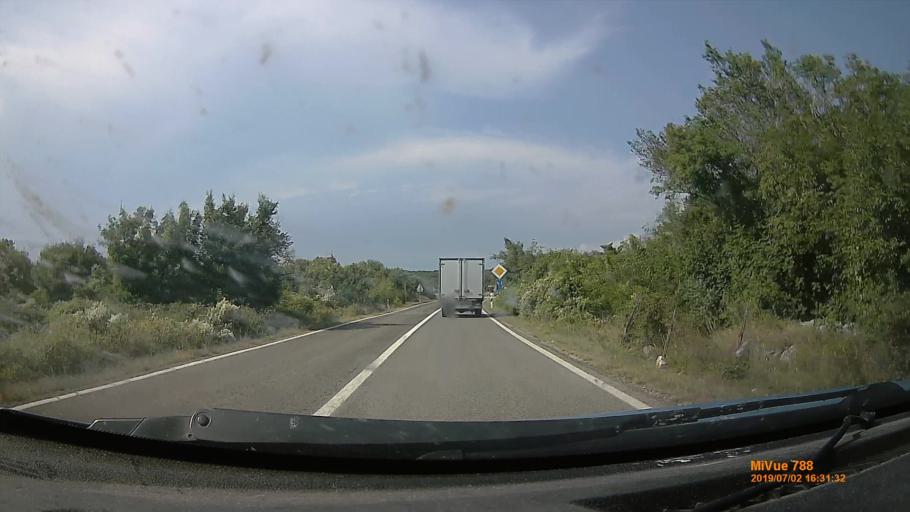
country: HR
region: Primorsko-Goranska
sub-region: Grad Krk
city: Krk
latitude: 45.0548
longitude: 14.4874
